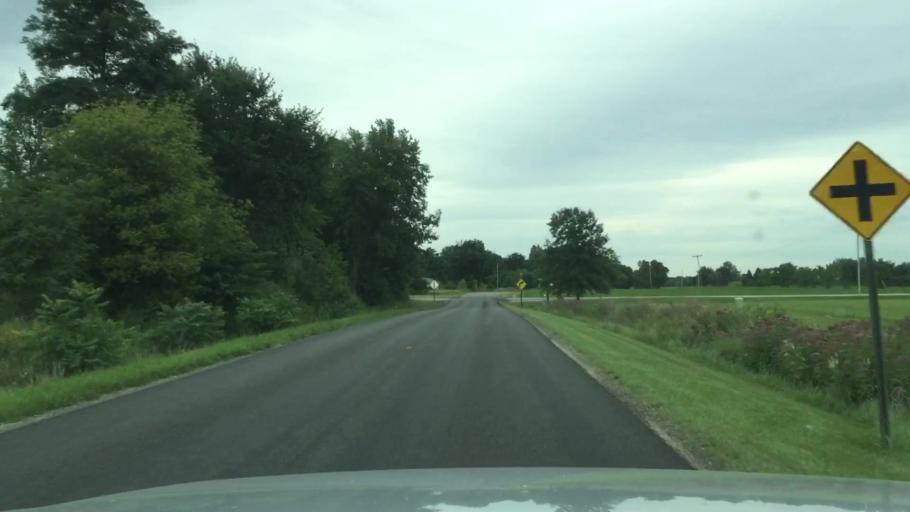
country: US
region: Michigan
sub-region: Shiawassee County
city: Durand
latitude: 42.8636
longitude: -84.0452
